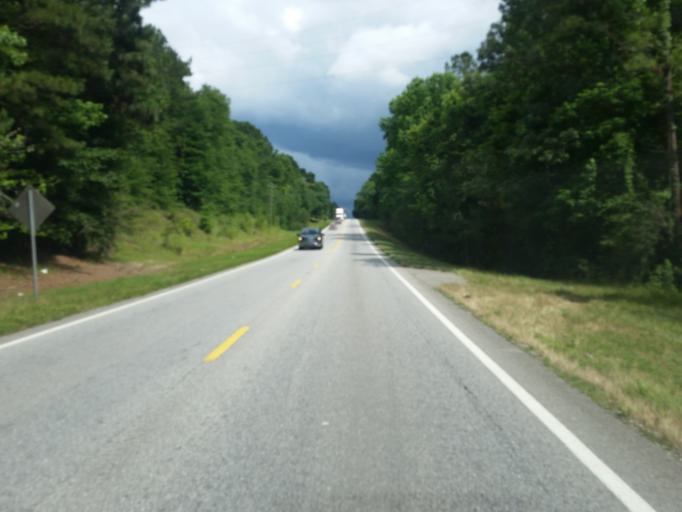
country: US
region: Mississippi
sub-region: Jackson County
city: Hurley
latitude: 30.8355
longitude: -88.3910
